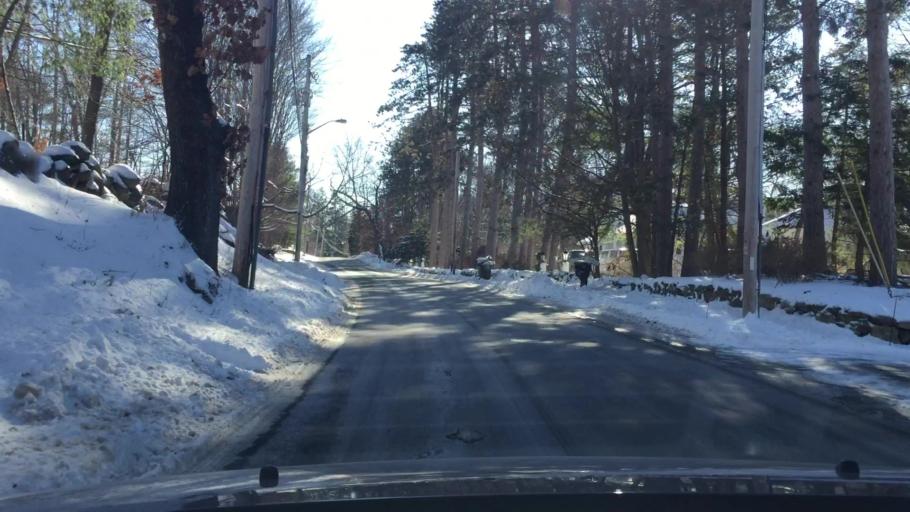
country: US
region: Massachusetts
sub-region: Essex County
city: North Andover
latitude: 42.6854
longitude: -71.0995
